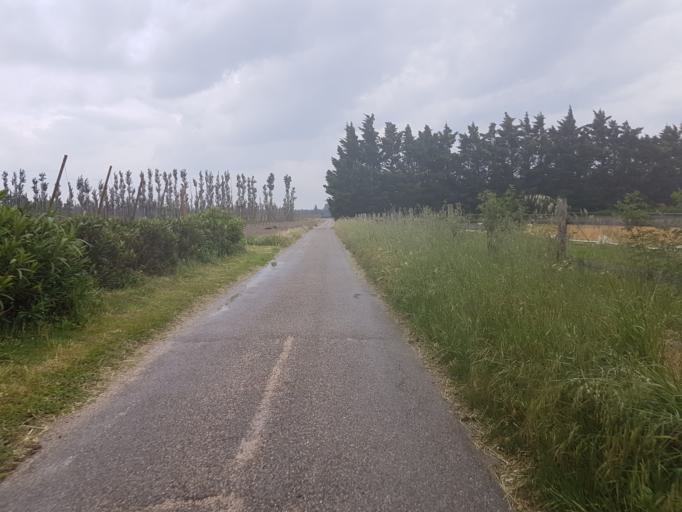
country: FR
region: Languedoc-Roussillon
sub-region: Departement du Gard
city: Villeneuve-les-Avignon
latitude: 43.9741
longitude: 4.8226
